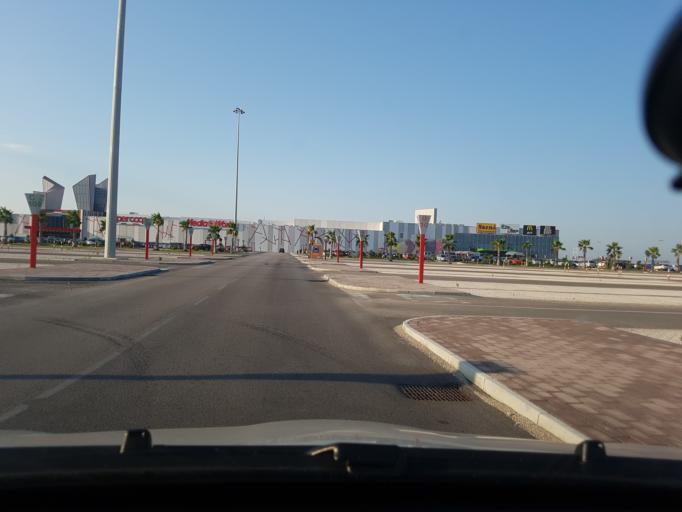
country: IT
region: Apulia
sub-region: Provincia di Foggia
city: Carapelle
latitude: 41.4136
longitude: 15.6516
